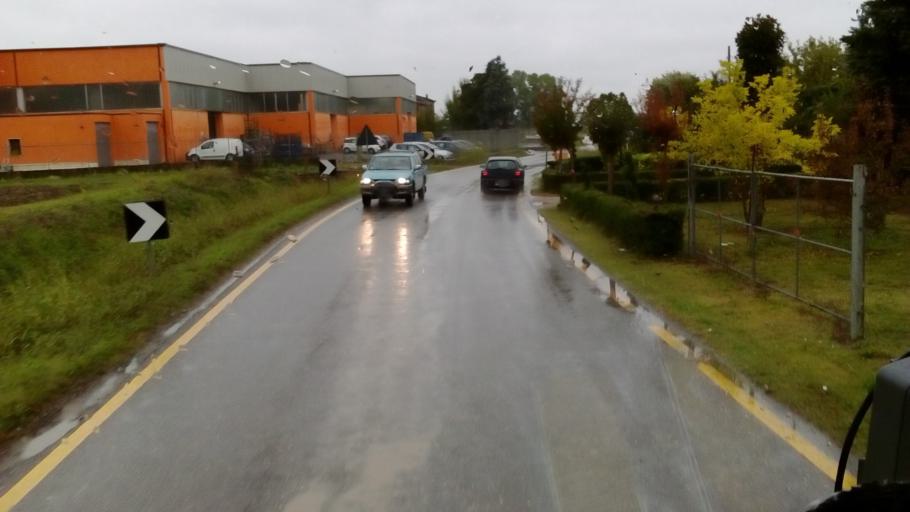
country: IT
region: Emilia-Romagna
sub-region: Provincia di Reggio Emilia
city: Luzzara
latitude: 44.9469
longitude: 10.7113
